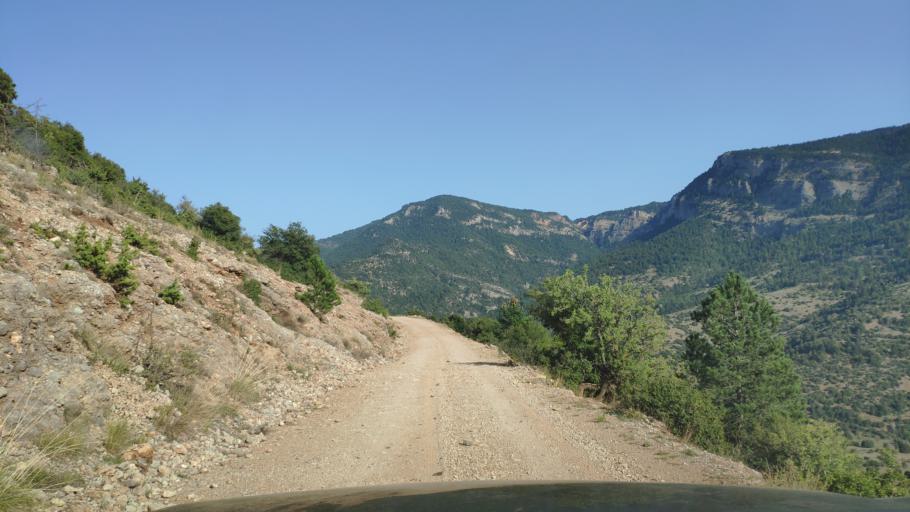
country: GR
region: West Greece
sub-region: Nomos Achaias
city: Aiyira
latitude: 37.9852
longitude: 22.3473
